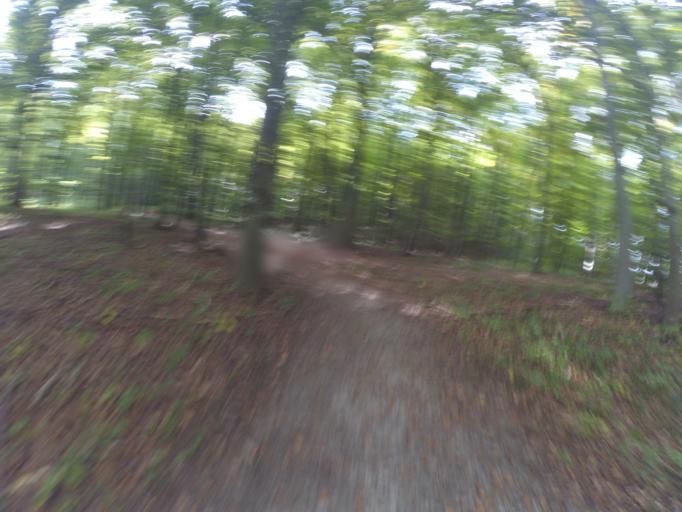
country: DE
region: Baden-Wuerttemberg
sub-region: Regierungsbezirk Stuttgart
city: Heubach
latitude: 48.7818
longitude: 9.9186
